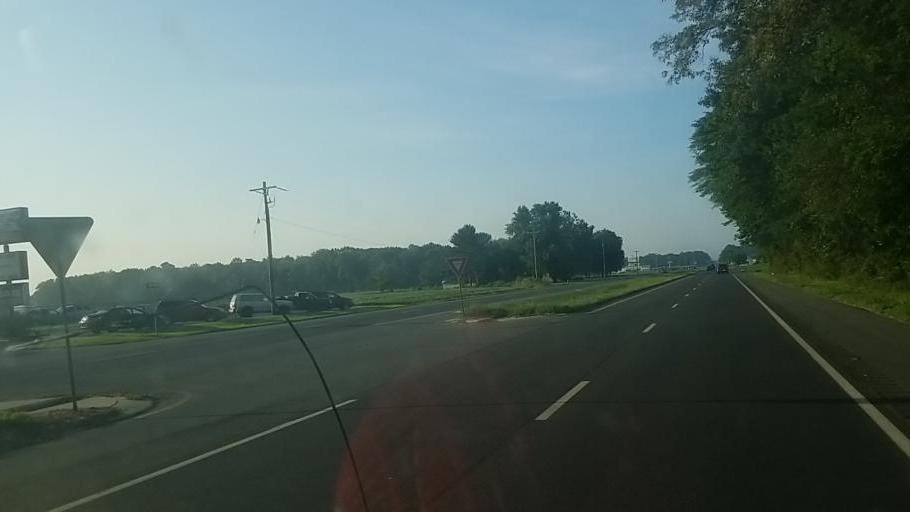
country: US
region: Delaware
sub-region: Sussex County
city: Selbyville
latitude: 38.4840
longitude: -75.2358
